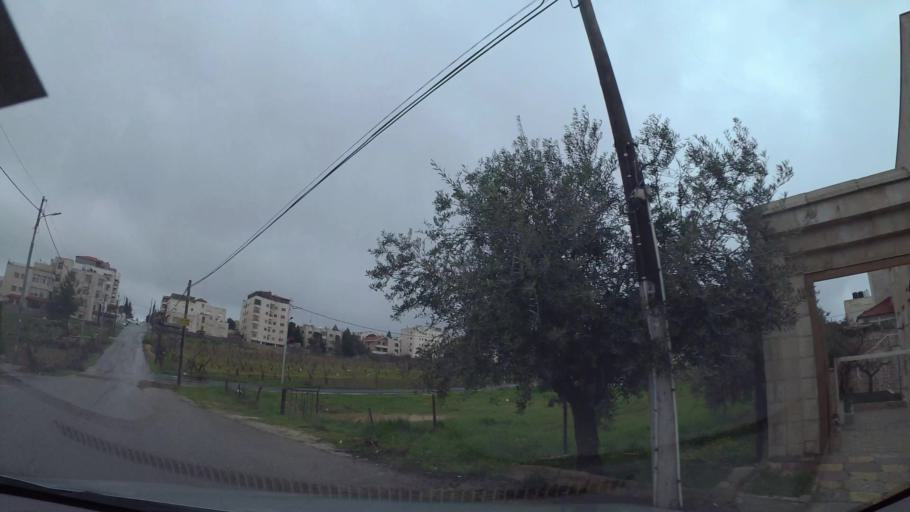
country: JO
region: Amman
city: Al Jubayhah
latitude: 32.0327
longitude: 35.8588
